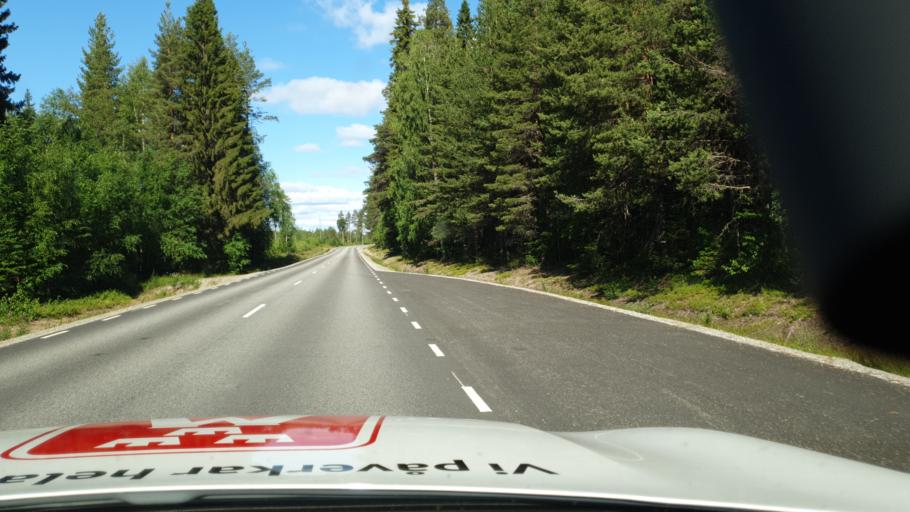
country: SE
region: Vaesterbotten
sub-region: Norsjo Kommun
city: Norsjoe
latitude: 64.6905
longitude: 19.2059
